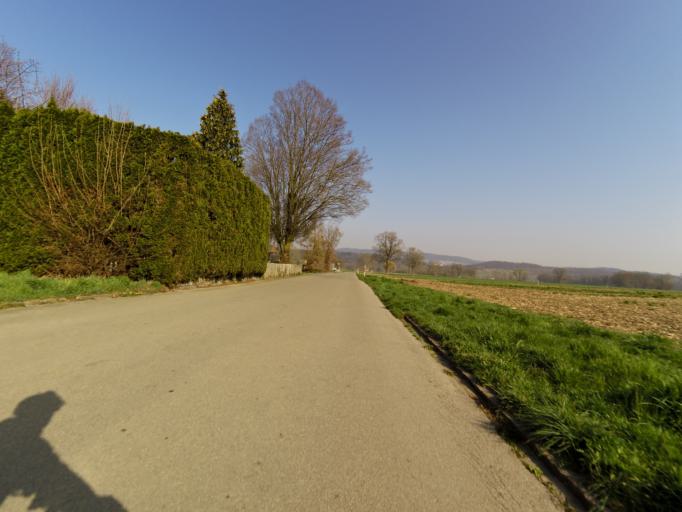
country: CH
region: Thurgau
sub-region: Frauenfeld District
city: Frauenfeld
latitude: 47.5737
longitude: 8.9135
